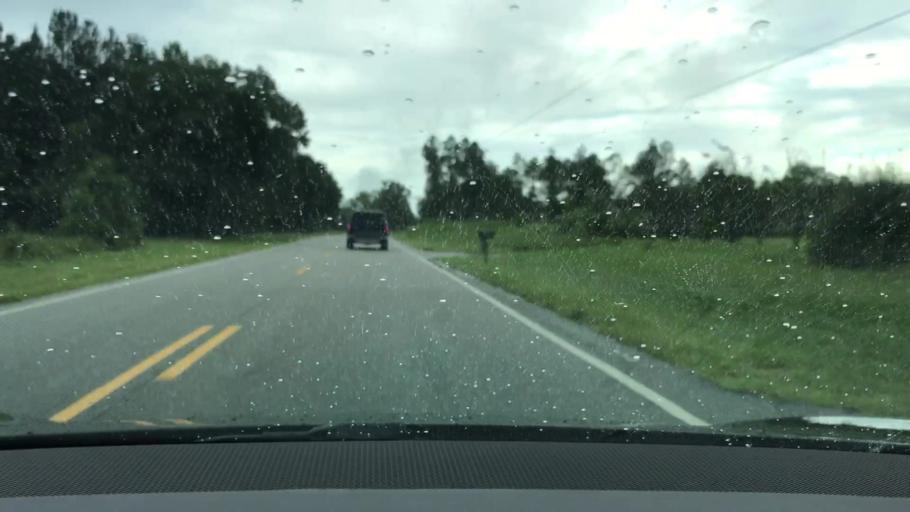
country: US
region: Alabama
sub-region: Geneva County
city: Samson
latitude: 31.1000
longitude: -86.1116
